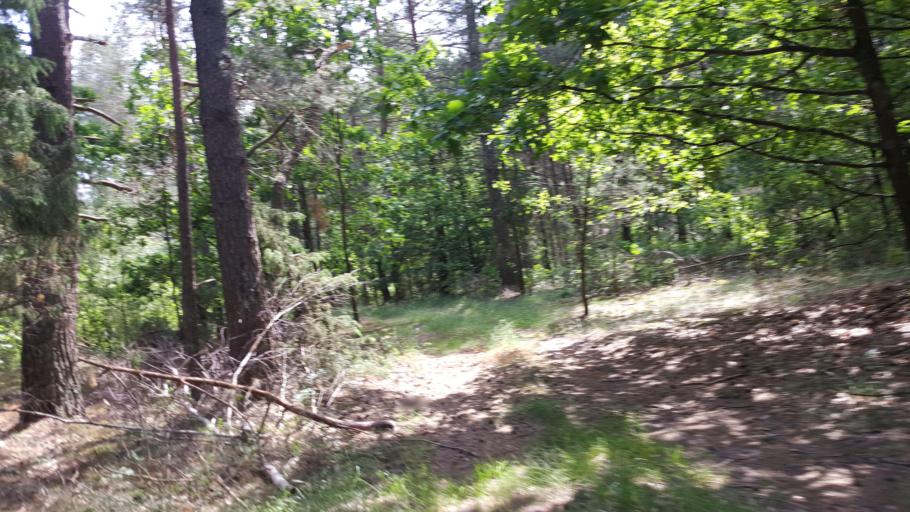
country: BY
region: Brest
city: Kamyanyuki
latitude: 52.5065
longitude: 23.8287
